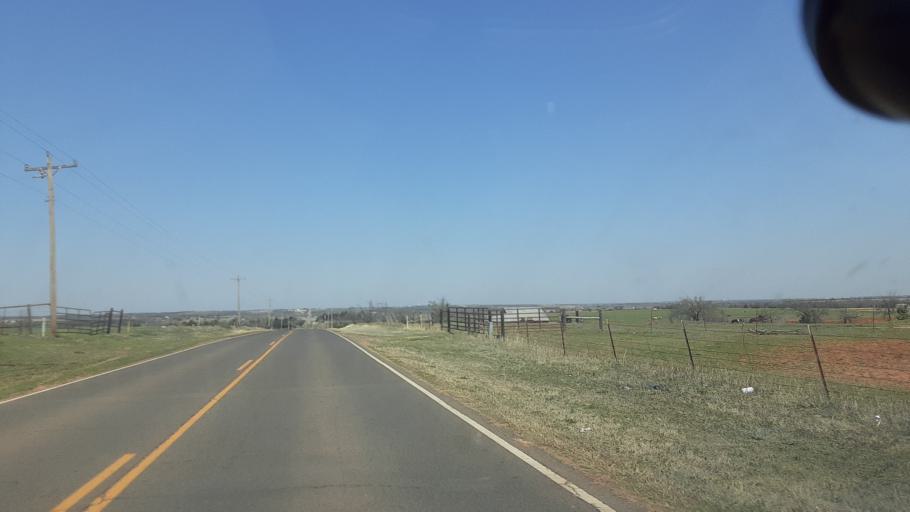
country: US
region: Oklahoma
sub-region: Logan County
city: Guthrie
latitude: 35.7903
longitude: -97.4783
